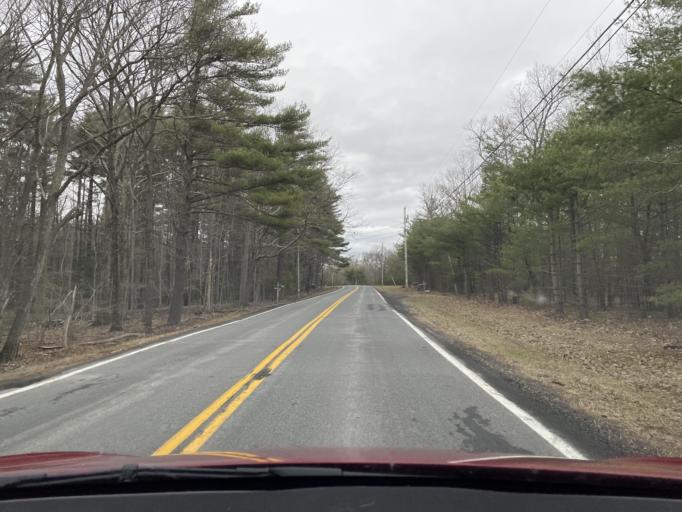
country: US
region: New York
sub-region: Ulster County
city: Zena
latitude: 42.0740
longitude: -74.0707
